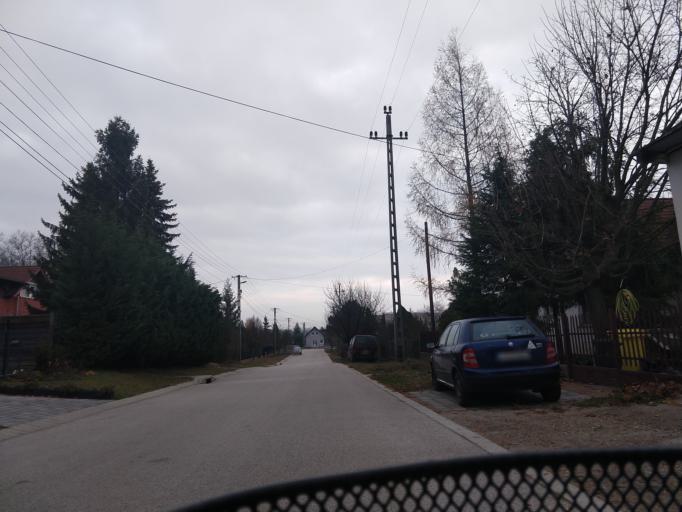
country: HU
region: Pest
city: Orbottyan
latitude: 47.6700
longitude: 19.2854
